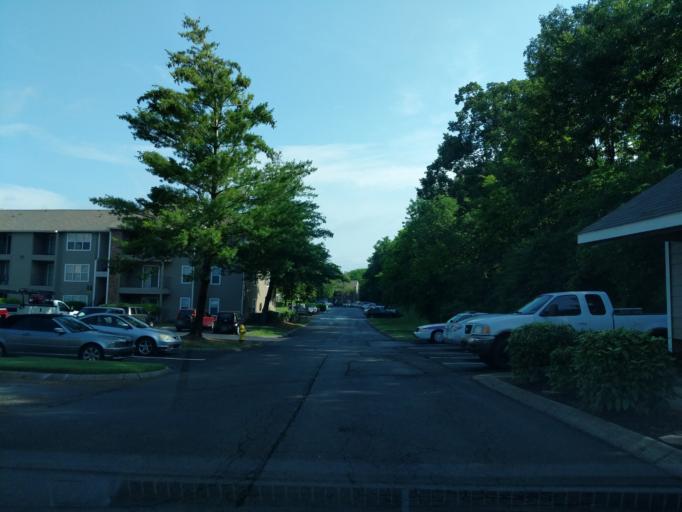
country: US
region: Tennessee
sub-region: Sumner County
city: Hendersonville
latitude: 36.3092
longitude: -86.6517
